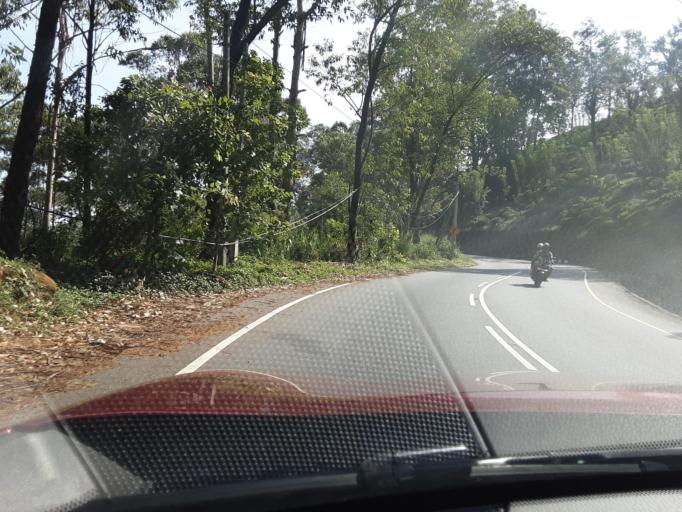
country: LK
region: Uva
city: Badulla
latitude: 6.9604
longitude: 81.1089
